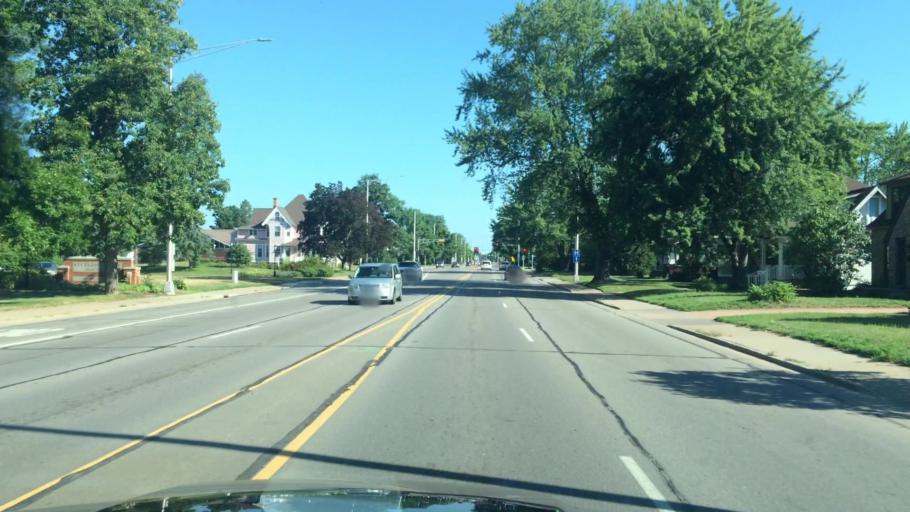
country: US
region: Wisconsin
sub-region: Marathon County
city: Wausau
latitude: 44.9434
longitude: -89.6198
